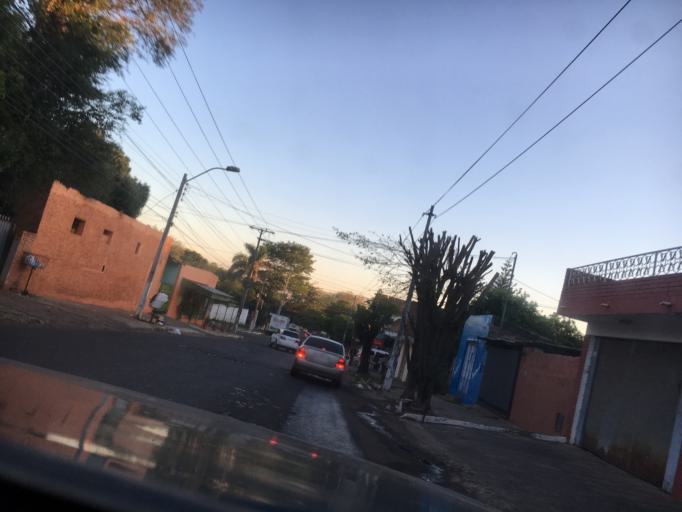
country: PY
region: Central
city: Lambare
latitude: -25.3245
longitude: -57.6109
